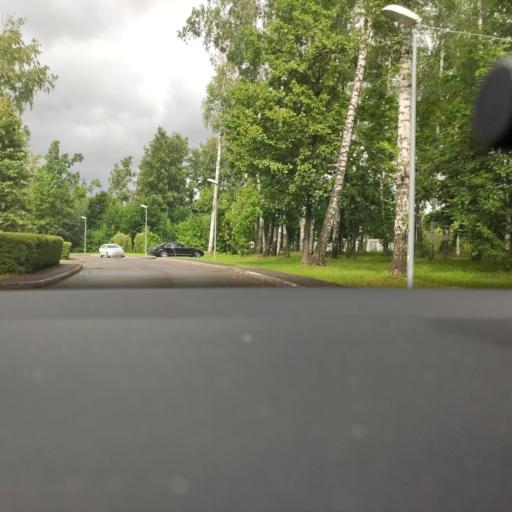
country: RU
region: Moscow
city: Rublevo
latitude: 55.8026
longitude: 37.3828
